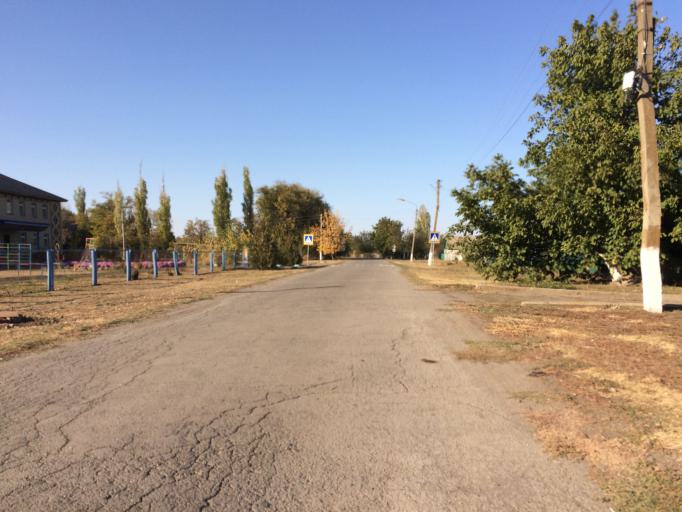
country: RU
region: Rostov
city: Tselina
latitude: 46.5174
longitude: 41.1840
